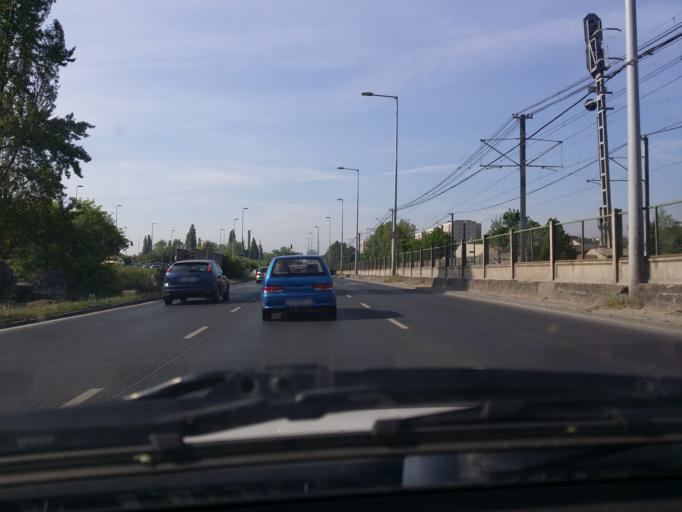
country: HU
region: Budapest
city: Budapest III. keruelet
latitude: 47.5632
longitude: 19.0480
